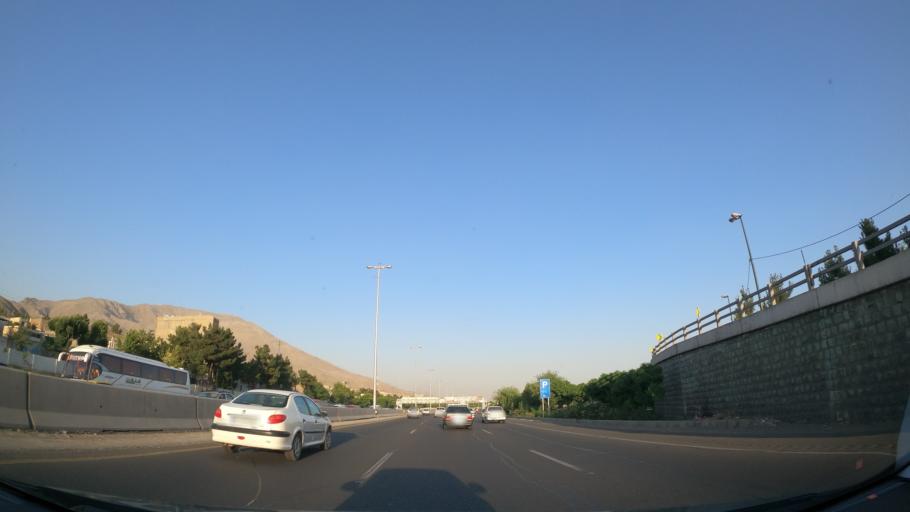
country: IR
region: Alborz
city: Karaj
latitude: 35.7877
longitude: 51.0220
